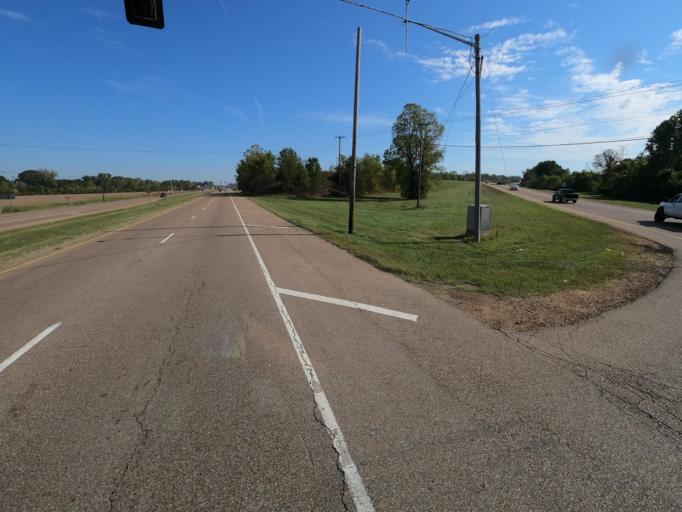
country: US
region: Tennessee
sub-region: Shelby County
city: Millington
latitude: 35.3300
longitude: -89.9220
